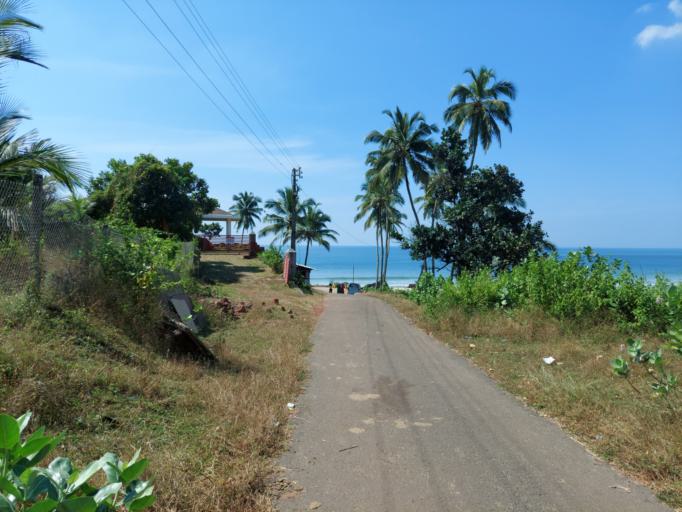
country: IN
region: Maharashtra
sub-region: Sindhudurg
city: Vengurla
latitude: 15.9186
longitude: 73.5684
